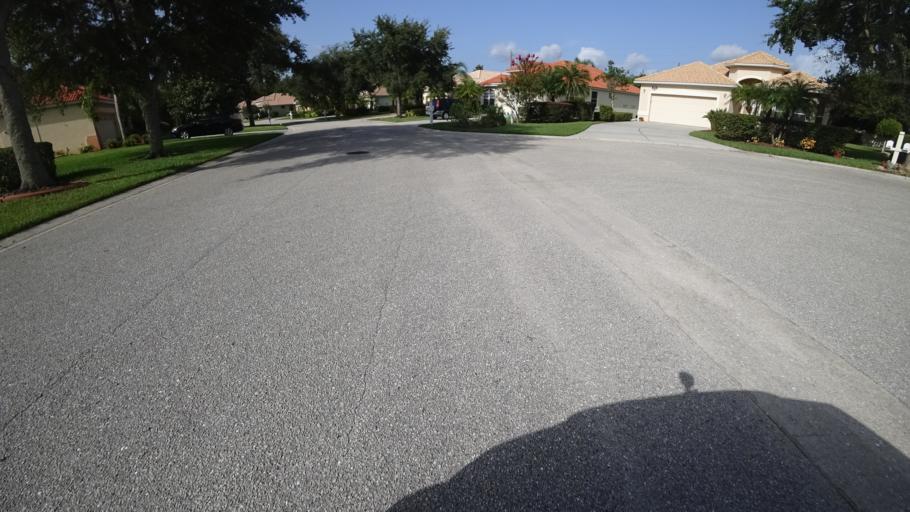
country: US
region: Florida
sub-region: Sarasota County
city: Desoto Lakes
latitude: 27.4319
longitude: -82.4704
